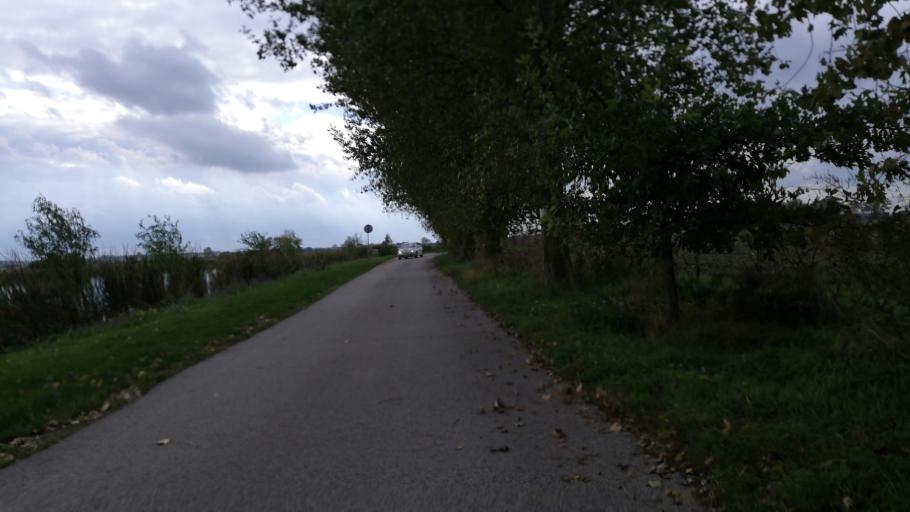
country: SK
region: Trnavsky
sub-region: Okres Skalica
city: Skalica
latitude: 48.8402
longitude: 17.1960
